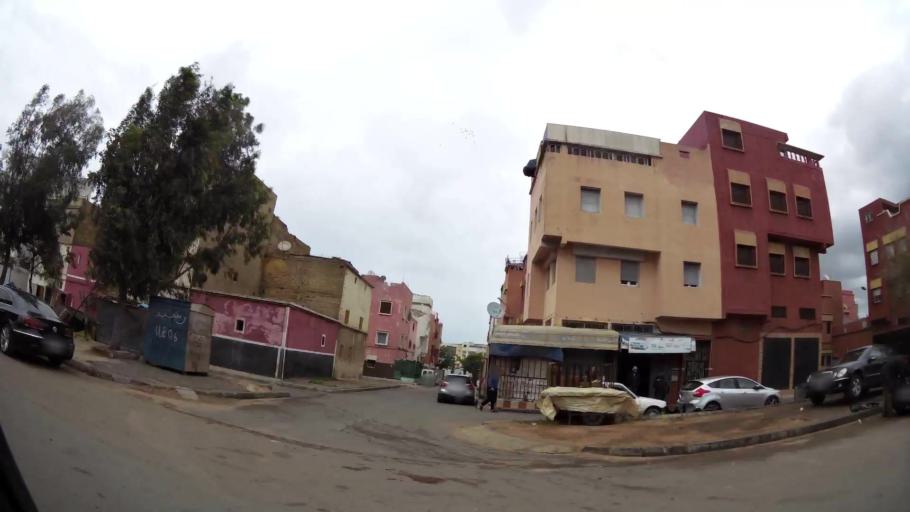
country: MA
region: Grand Casablanca
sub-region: Mediouna
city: Tit Mellil
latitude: 33.5558
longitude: -7.5510
